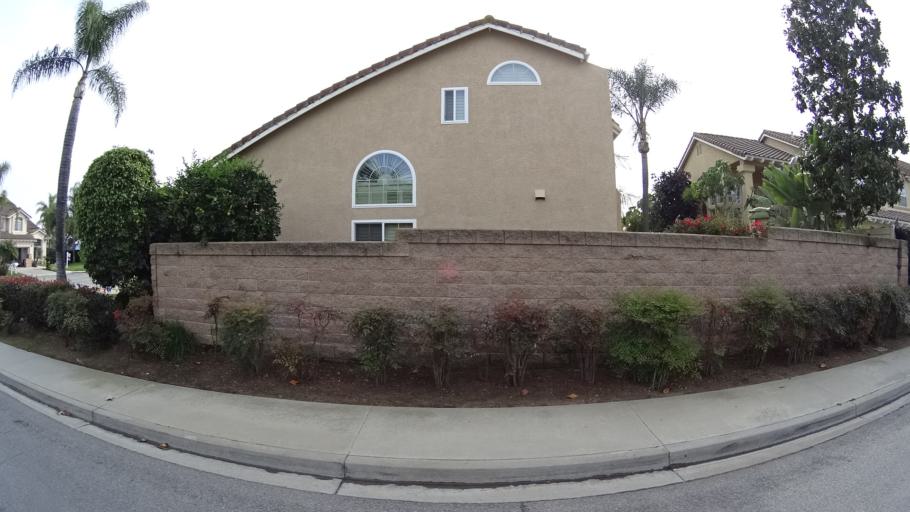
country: US
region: California
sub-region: Orange County
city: Laguna Woods
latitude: 33.5897
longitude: -117.7350
